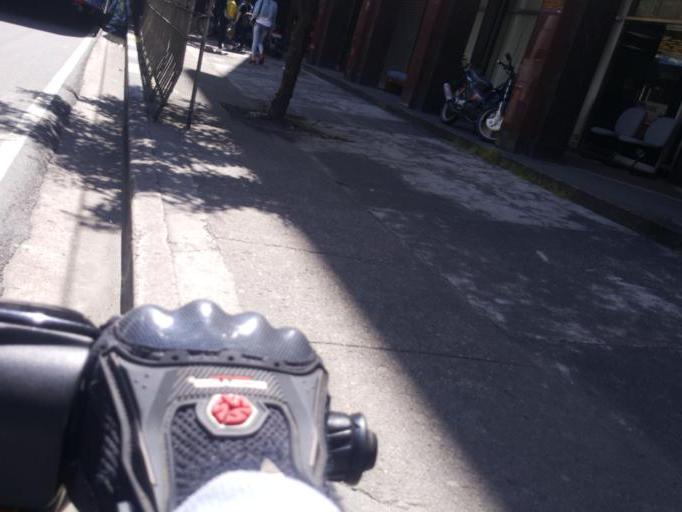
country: PH
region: Metro Manila
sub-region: Makati City
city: Makati City
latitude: 14.5594
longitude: 121.0104
